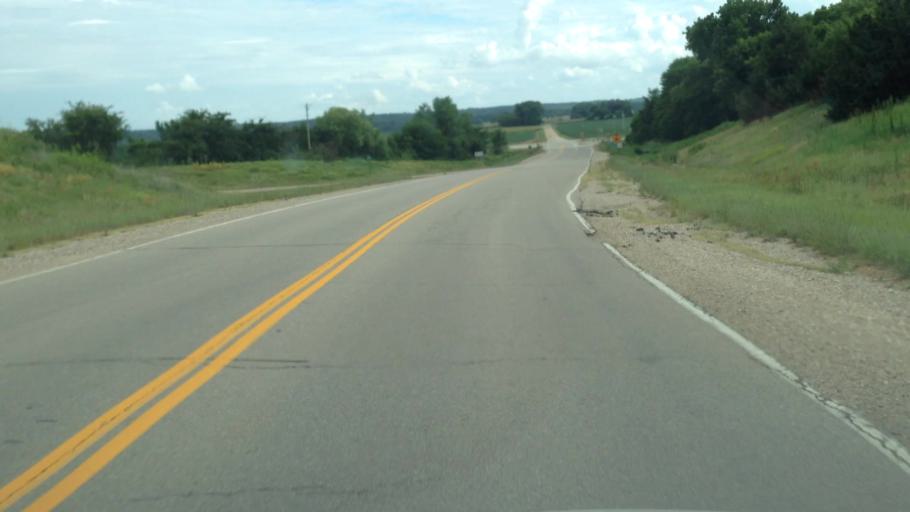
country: US
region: Kansas
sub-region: Jefferson County
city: Oskaloosa
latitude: 39.0897
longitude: -95.4739
